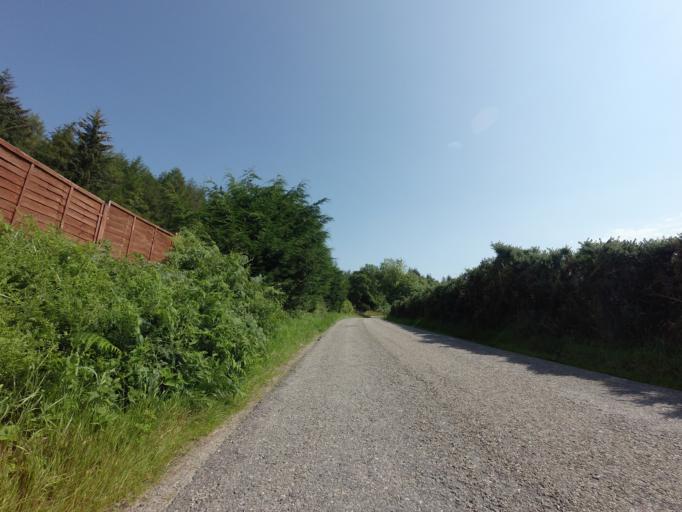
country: GB
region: Scotland
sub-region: Highland
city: Invergordon
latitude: 57.7583
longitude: -4.1310
